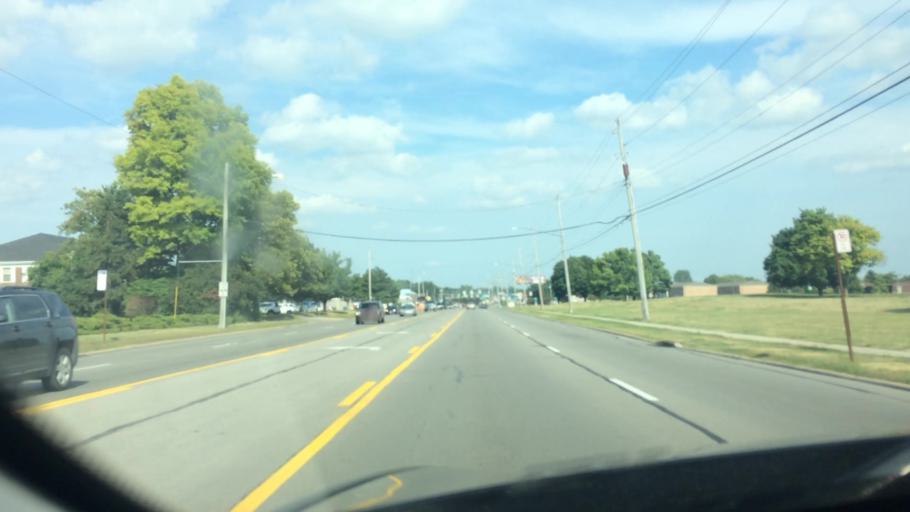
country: US
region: Ohio
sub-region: Lucas County
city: Maumee
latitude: 41.5943
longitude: -83.6512
